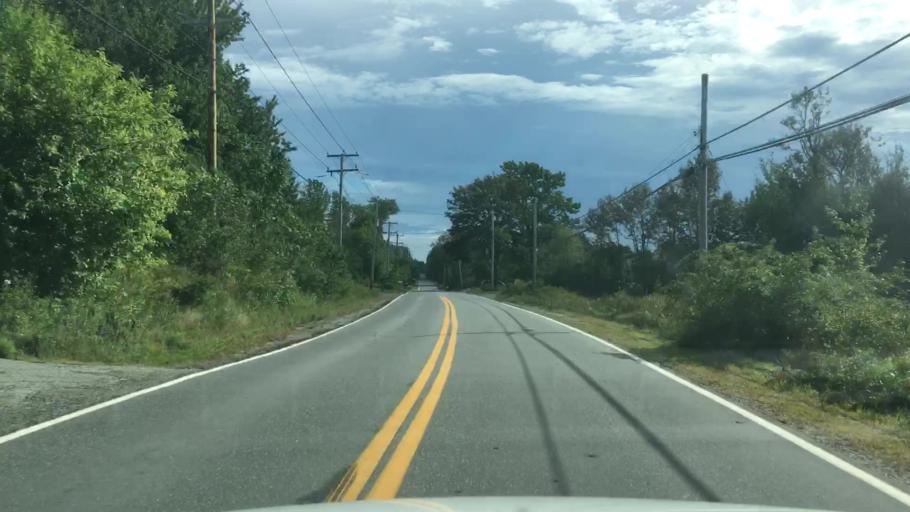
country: US
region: Maine
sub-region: Hancock County
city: Ellsworth
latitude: 44.4994
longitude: -68.4205
